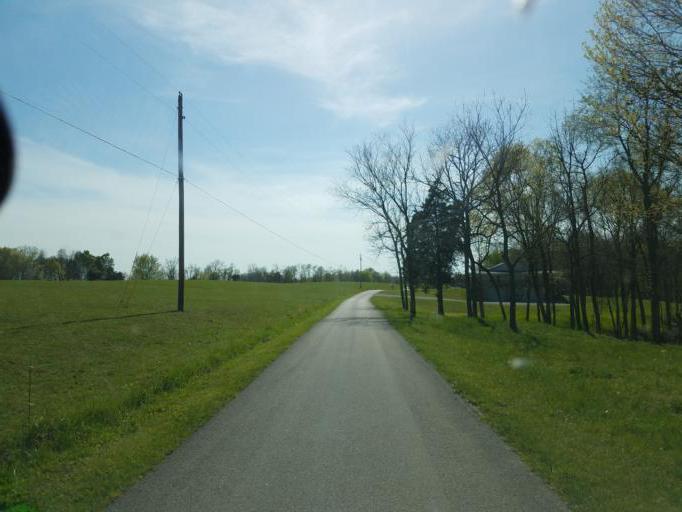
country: US
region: Kentucky
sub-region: Barren County
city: Cave City
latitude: 37.1234
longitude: -86.0989
